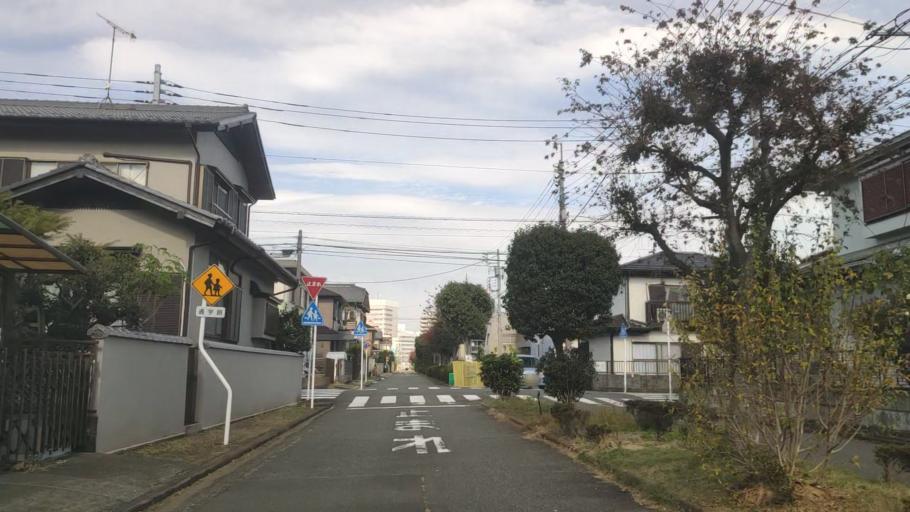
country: JP
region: Kanagawa
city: Atsugi
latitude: 35.4326
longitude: 139.3640
